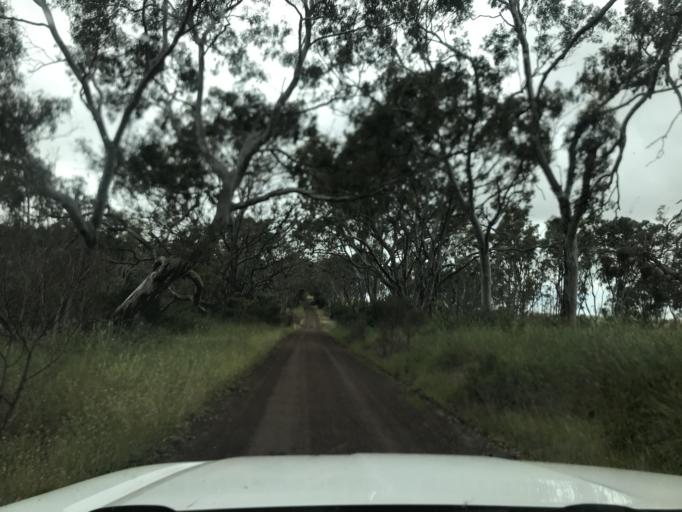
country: AU
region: South Australia
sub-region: Wattle Range
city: Penola
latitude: -37.2345
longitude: 141.4365
